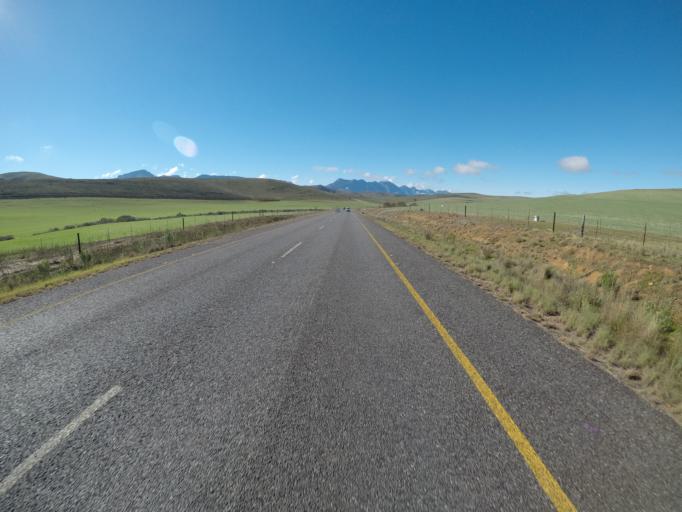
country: ZA
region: Western Cape
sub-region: Overberg District Municipality
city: Caledon
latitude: -34.0955
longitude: 19.5391
